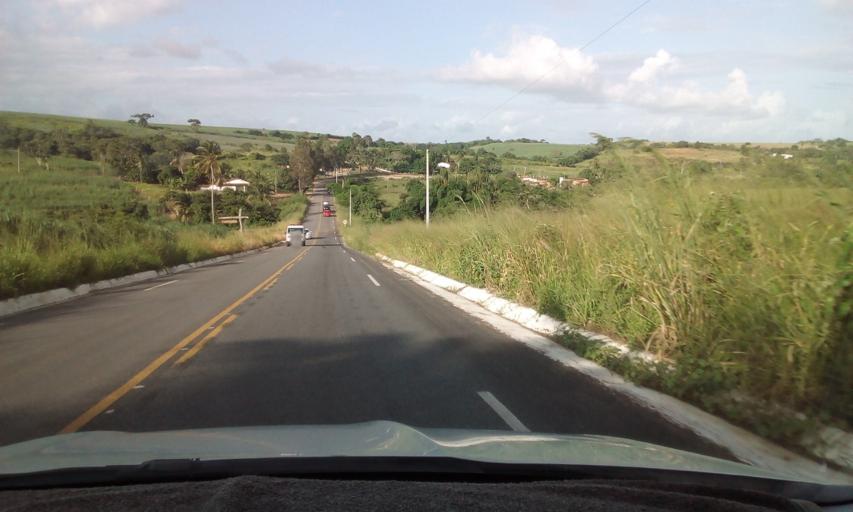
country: BR
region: Paraiba
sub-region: Mamanguape
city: Mamanguape
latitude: -6.8098
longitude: -35.1995
